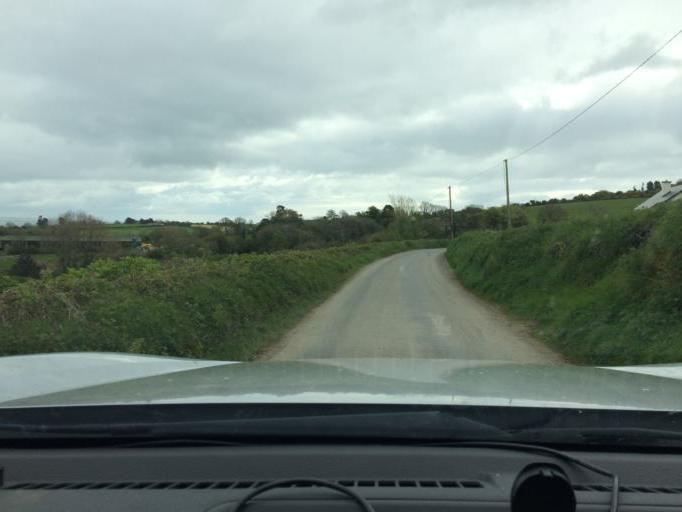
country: IE
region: Munster
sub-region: Waterford
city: Dungarvan
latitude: 52.0549
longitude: -7.6274
